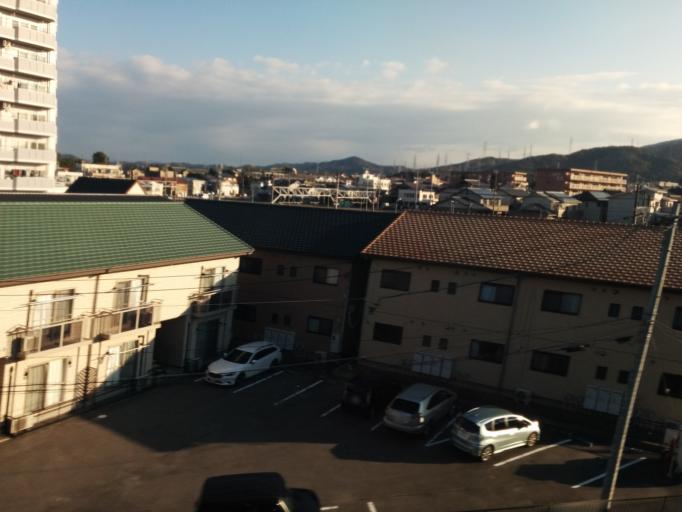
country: JP
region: Aichi
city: Gamagori
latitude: 34.8583
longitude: 137.1638
